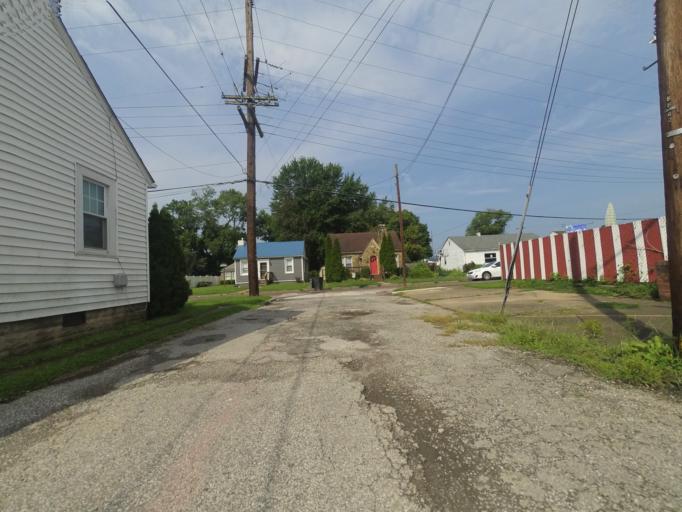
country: US
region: West Virginia
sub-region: Cabell County
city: Huntington
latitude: 38.4113
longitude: -82.4584
